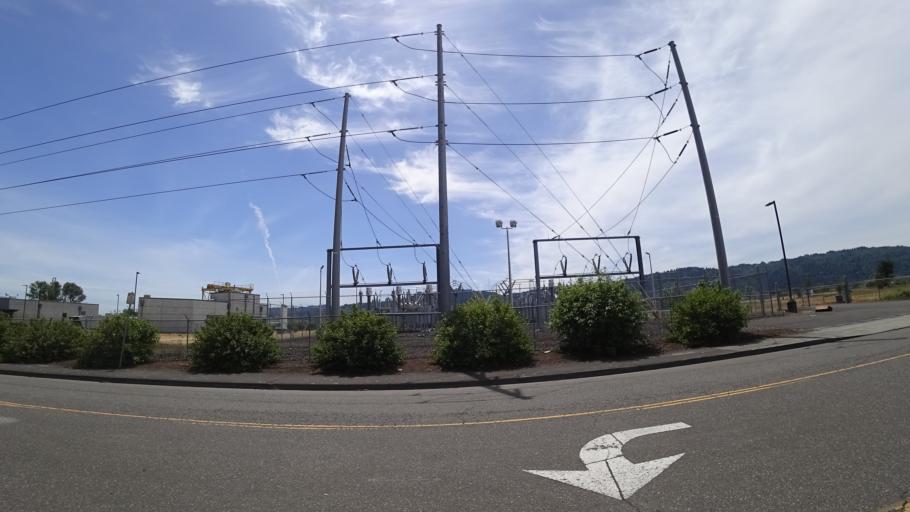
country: US
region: Oregon
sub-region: Multnomah County
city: Portland
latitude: 45.5542
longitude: -122.6967
